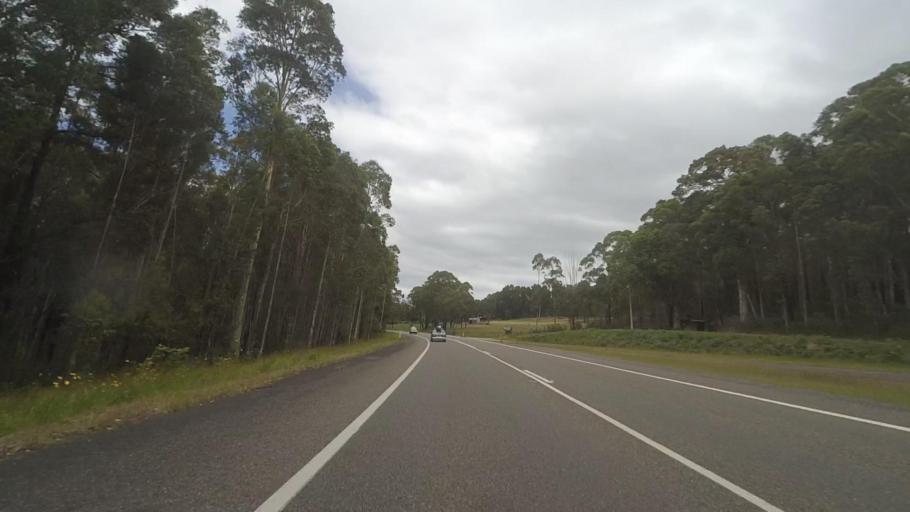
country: AU
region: New South Wales
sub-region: Shoalhaven Shire
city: Milton
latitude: -35.1324
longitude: 150.4659
